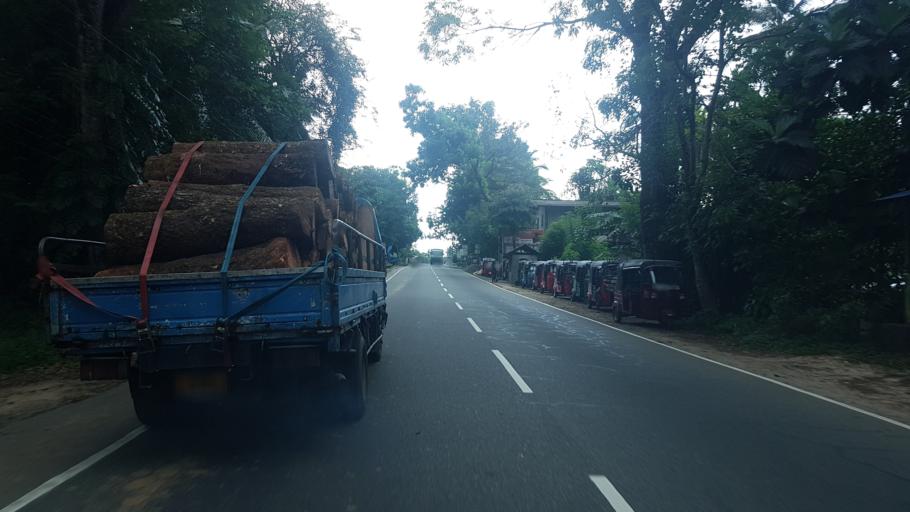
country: LK
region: Western
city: Hanwella Ihala
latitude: 7.0186
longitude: 80.2633
